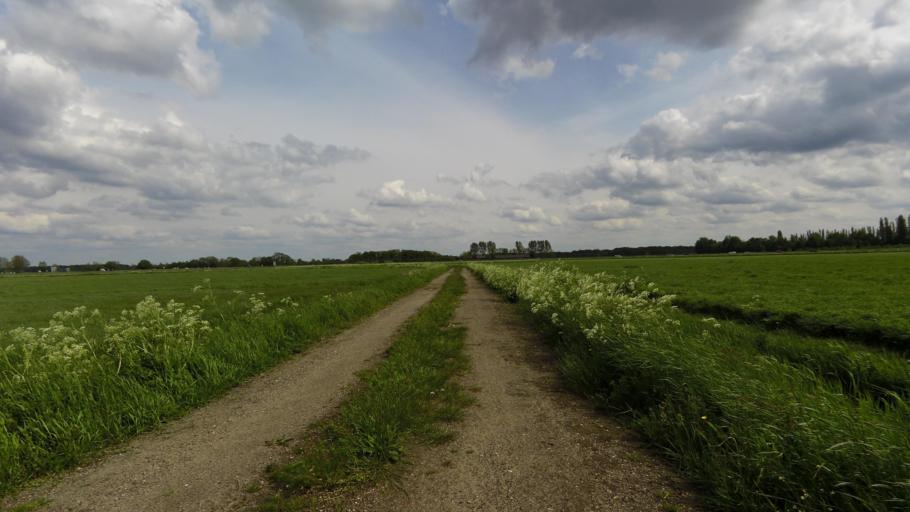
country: NL
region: Gelderland
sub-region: Gemeente Nijkerk
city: Nijkerk
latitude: 52.2485
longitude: 5.4835
